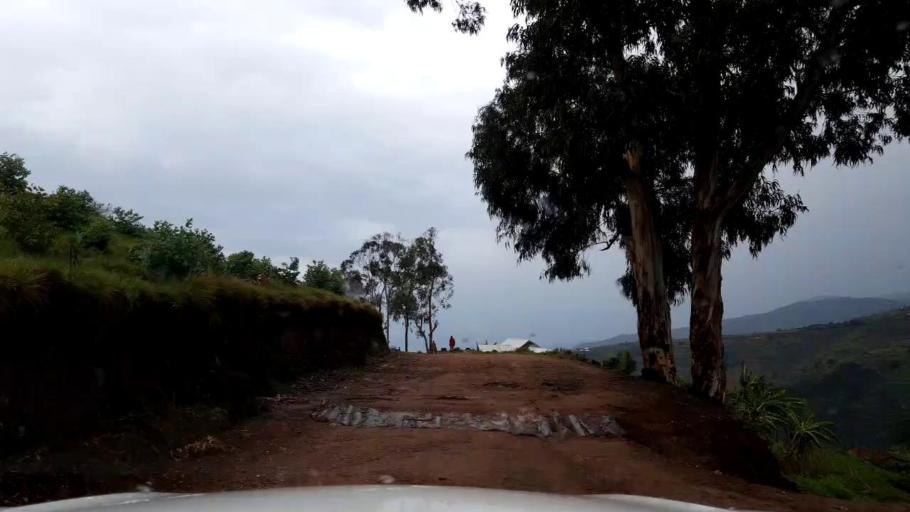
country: RW
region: Western Province
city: Kibuye
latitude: -2.0221
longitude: 29.4580
